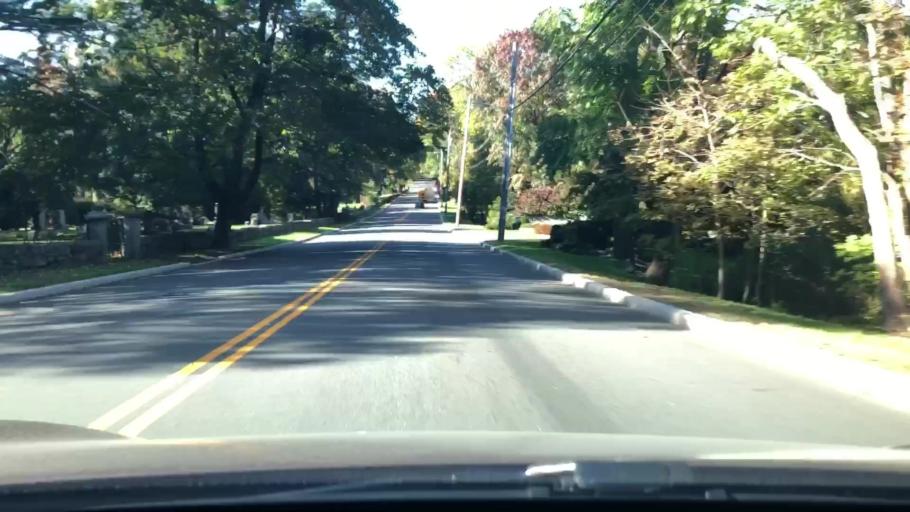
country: US
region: New York
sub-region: Westchester County
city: Rye
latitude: 40.9797
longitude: -73.6993
